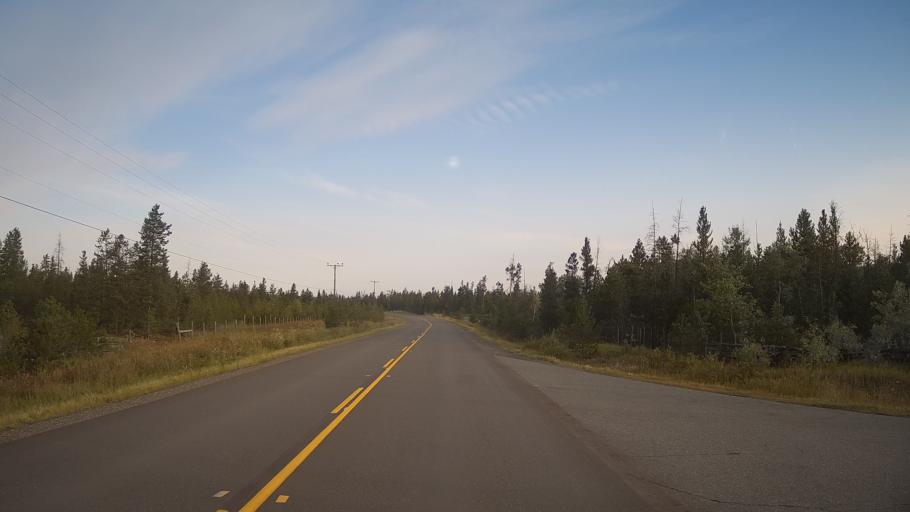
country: CA
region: British Columbia
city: Hanceville
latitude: 52.1350
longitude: -123.7012
